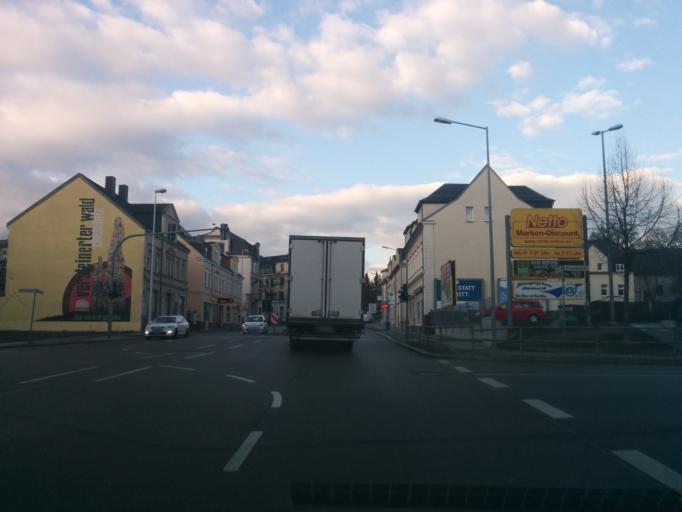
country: DE
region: Saxony
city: Hilbersdorf
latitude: 50.8508
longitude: 12.9456
